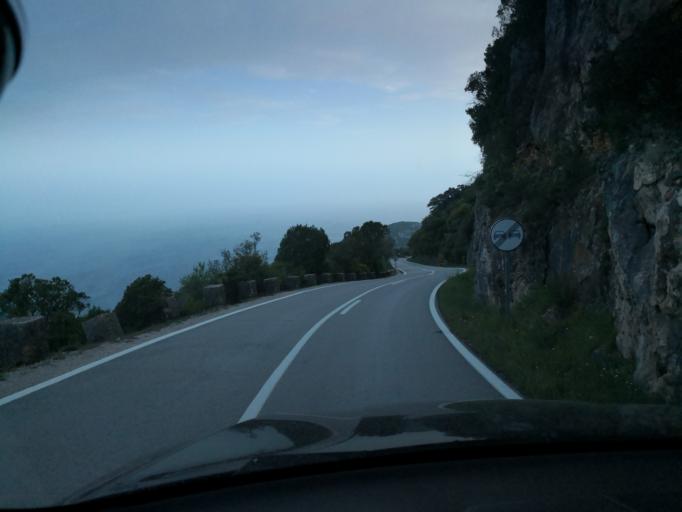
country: PT
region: Setubal
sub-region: Palmela
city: Quinta do Anjo
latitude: 38.4779
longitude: -8.9937
